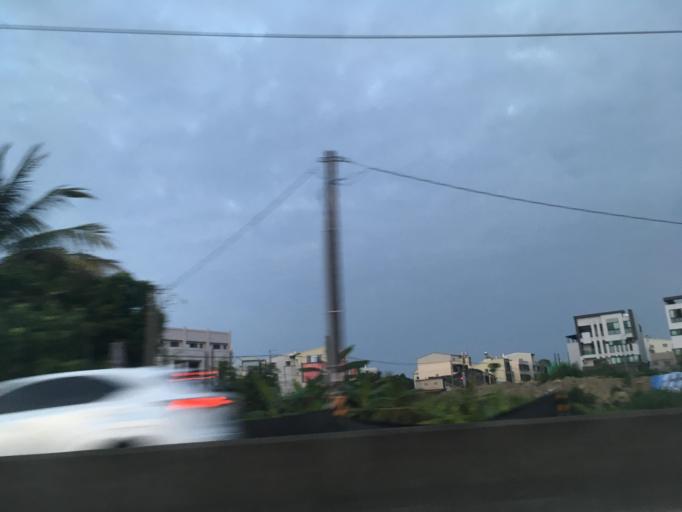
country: TW
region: Taiwan
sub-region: Chiayi
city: Jiayi Shi
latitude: 23.6013
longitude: 120.4497
